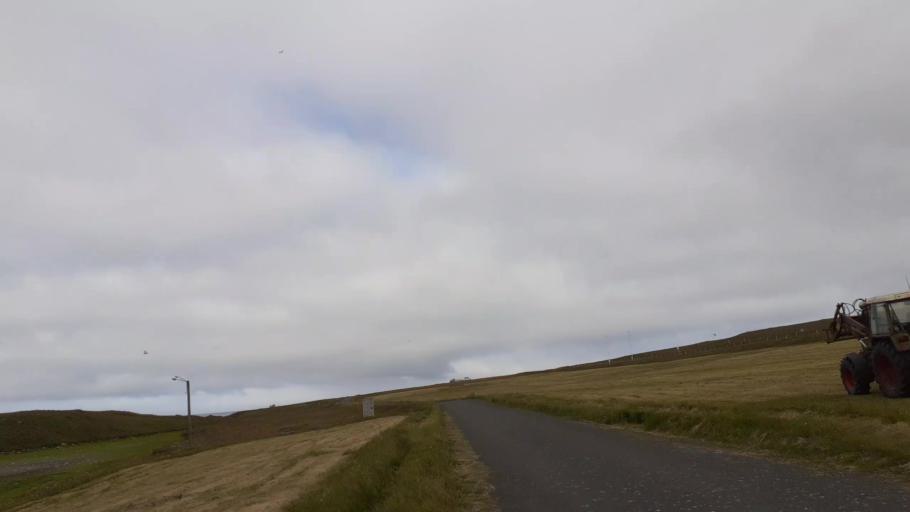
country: IS
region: Northeast
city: Dalvik
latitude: 66.5415
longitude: -18.0163
